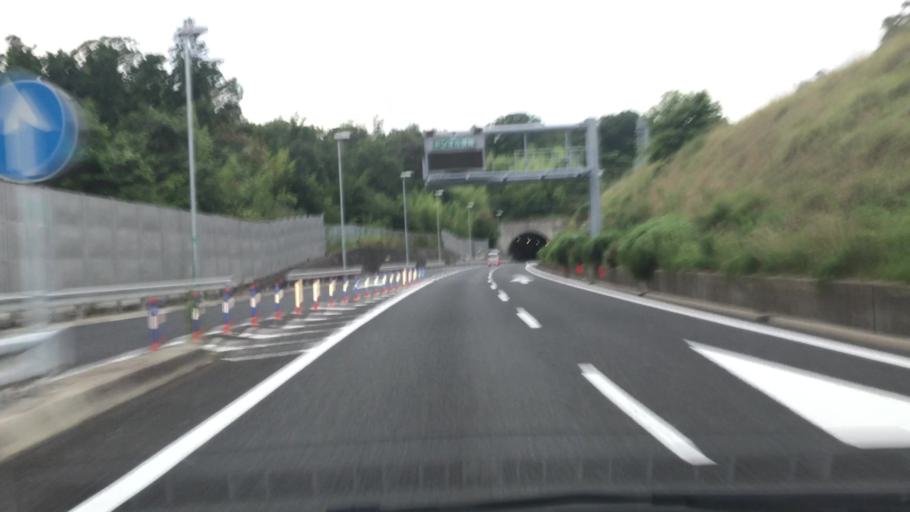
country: JP
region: Hyogo
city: Sandacho
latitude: 34.8120
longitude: 135.2474
